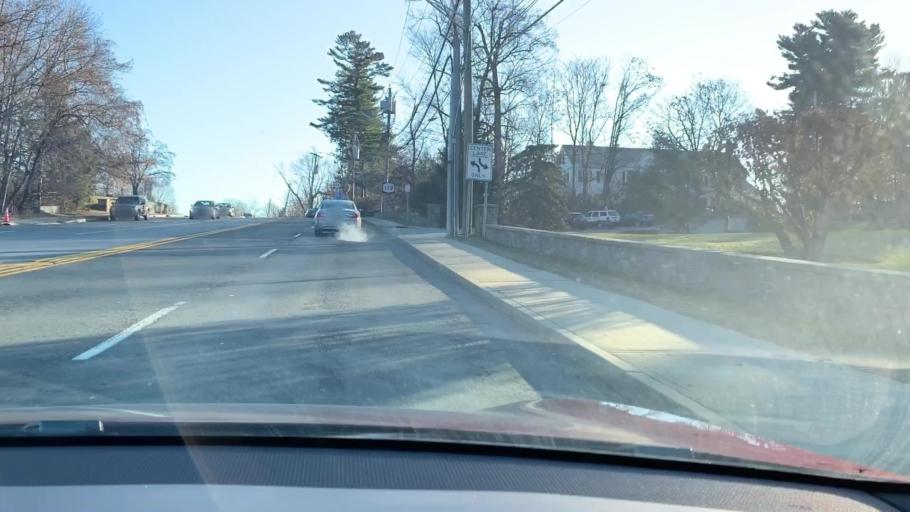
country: US
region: New York
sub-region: Westchester County
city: Tarrytown
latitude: 41.0636
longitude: -73.8609
